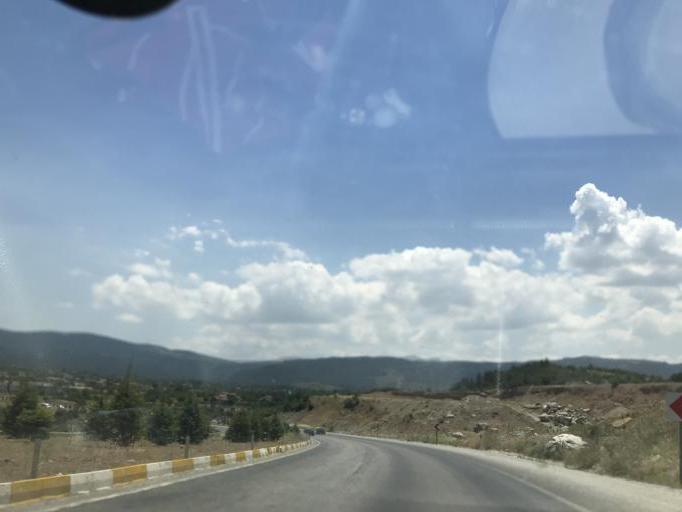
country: TR
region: Denizli
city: Honaz
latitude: 37.7008
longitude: 29.2002
